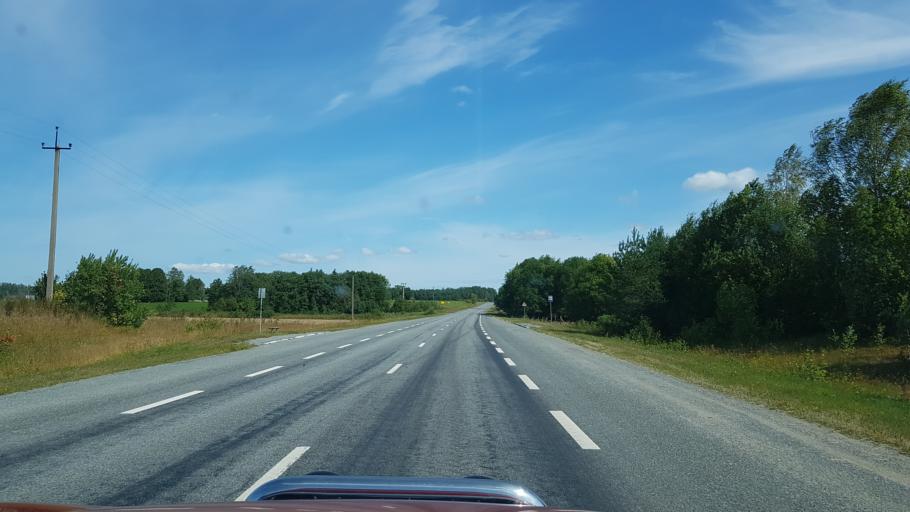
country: EE
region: Jaervamaa
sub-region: Jaerva-Jaani vald
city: Jarva-Jaani
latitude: 59.0795
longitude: 25.9613
